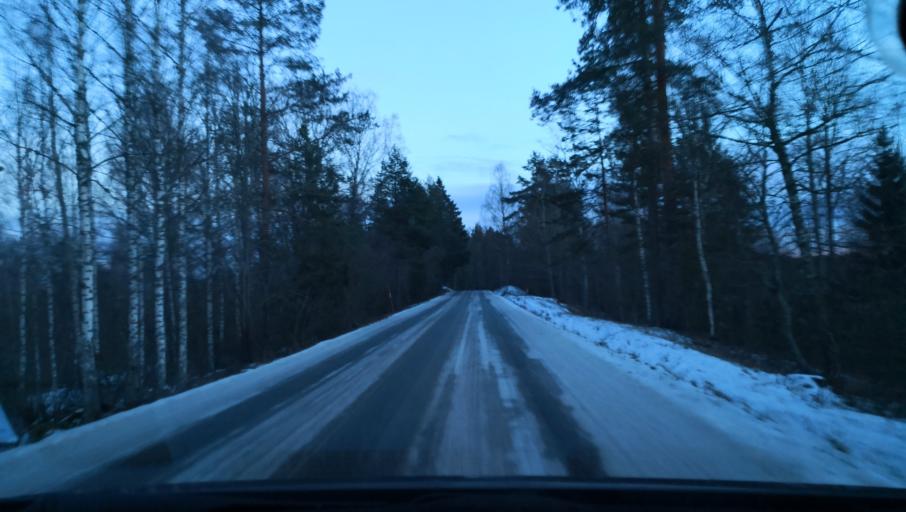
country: SE
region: Soedermanland
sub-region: Katrineholms Kommun
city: Katrineholm
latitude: 59.0830
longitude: 16.2272
